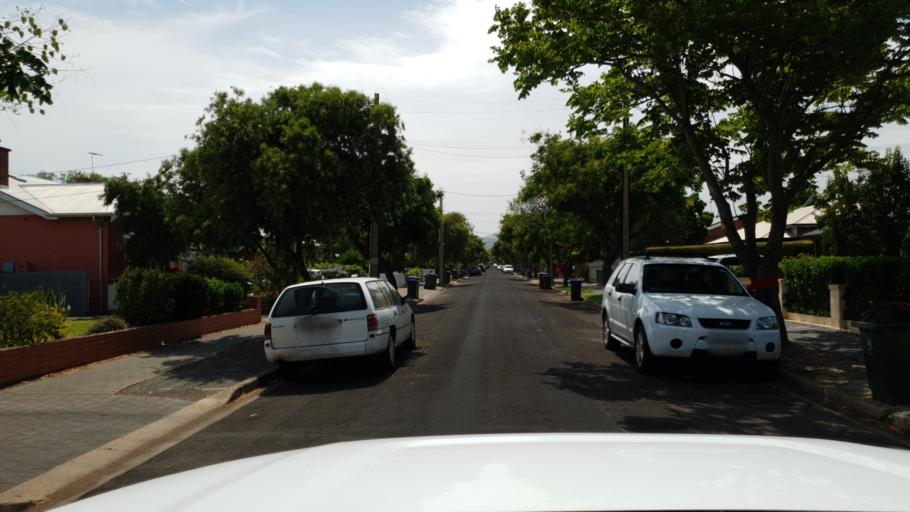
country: AU
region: South Australia
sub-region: Mitcham
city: Clarence Gardens
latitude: -34.9727
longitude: 138.5832
